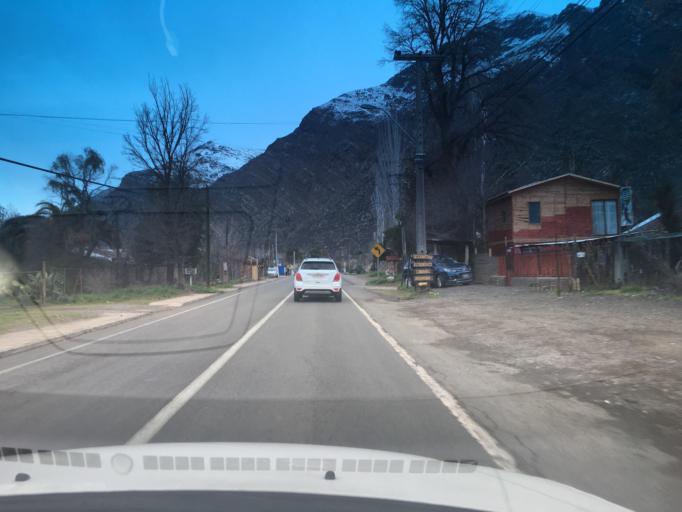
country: CL
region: Santiago Metropolitan
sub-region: Provincia de Cordillera
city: Puente Alto
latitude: -33.7168
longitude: -70.3312
